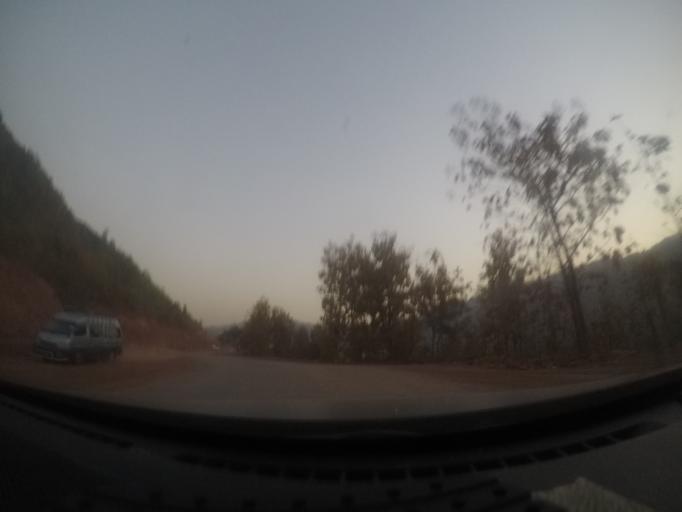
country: MM
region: Mandalay
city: Yamethin
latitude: 20.7140
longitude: 96.5001
